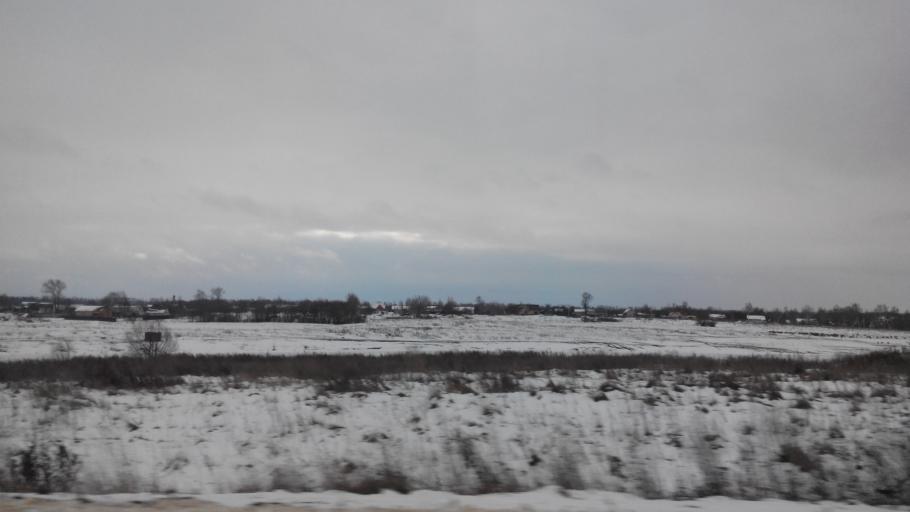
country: RU
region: Tula
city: Mayskiy
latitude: 53.9814
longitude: 38.2220
